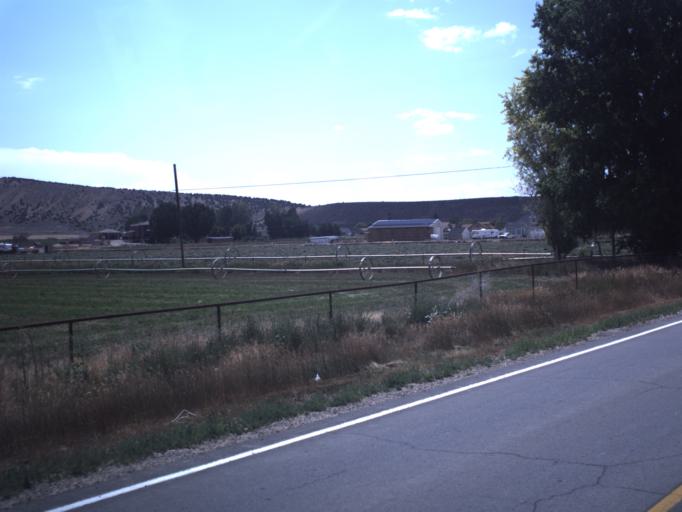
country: US
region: Utah
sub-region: Uintah County
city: Maeser
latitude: 40.4627
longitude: -109.6009
